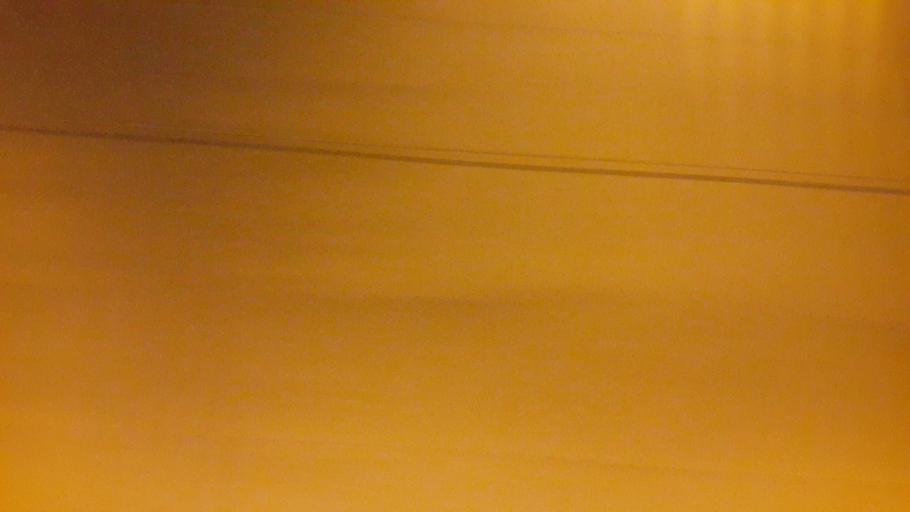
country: TR
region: Nigde
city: Ciftehan
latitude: 37.5236
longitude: 34.8168
